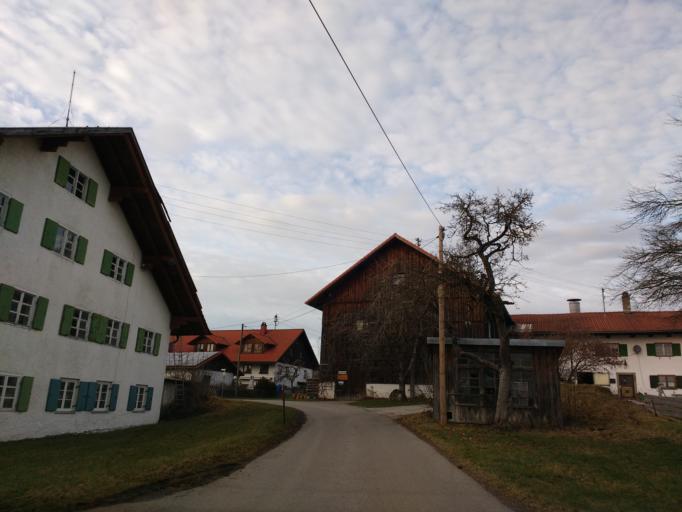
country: DE
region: Bavaria
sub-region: Swabia
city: Wildpoldsried
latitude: 47.7979
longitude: 10.4078
